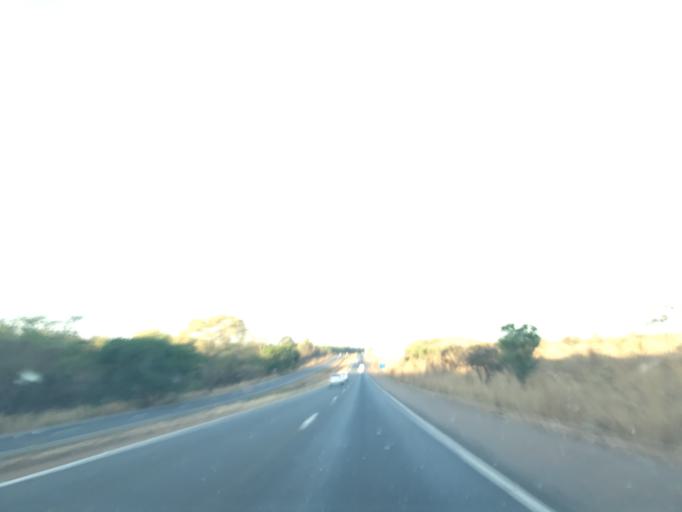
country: BR
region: Goias
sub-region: Anapolis
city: Anapolis
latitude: -16.3278
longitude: -48.8830
